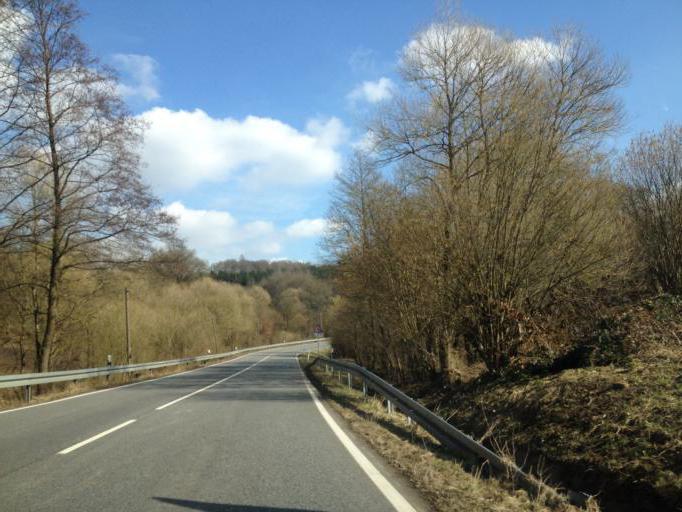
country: DE
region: Rheinland-Pfalz
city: Selchenbach
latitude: 49.4795
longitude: 7.2673
